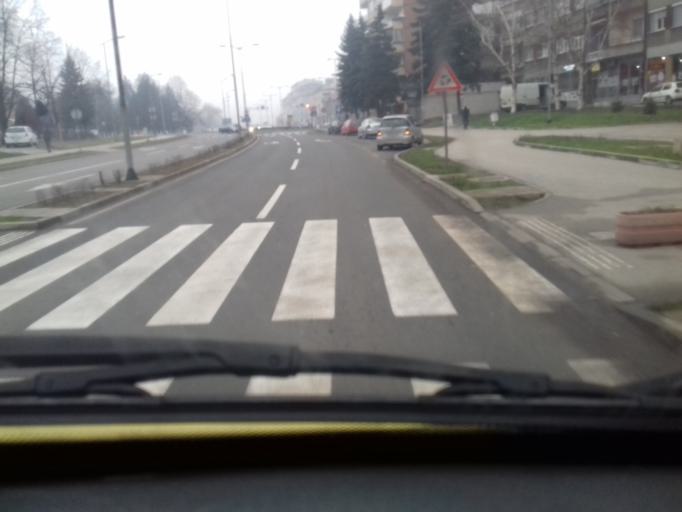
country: BA
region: Federation of Bosnia and Herzegovina
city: Zenica
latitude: 44.1994
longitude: 17.9047
